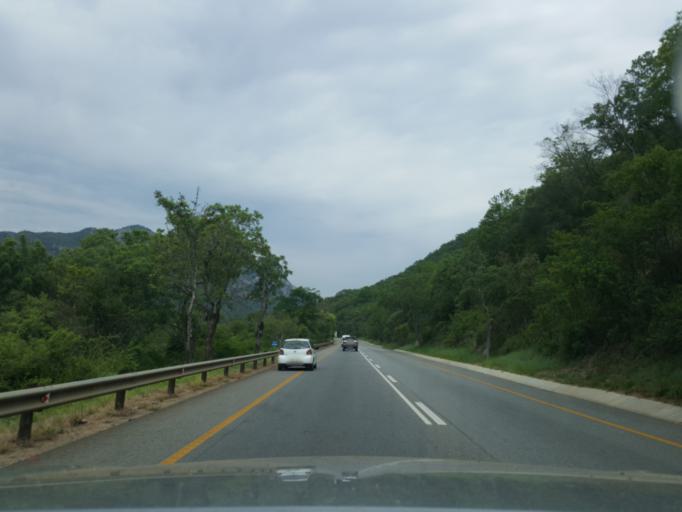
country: SZ
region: Hhohho
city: Ntfonjeni
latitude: -25.5269
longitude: 31.2719
